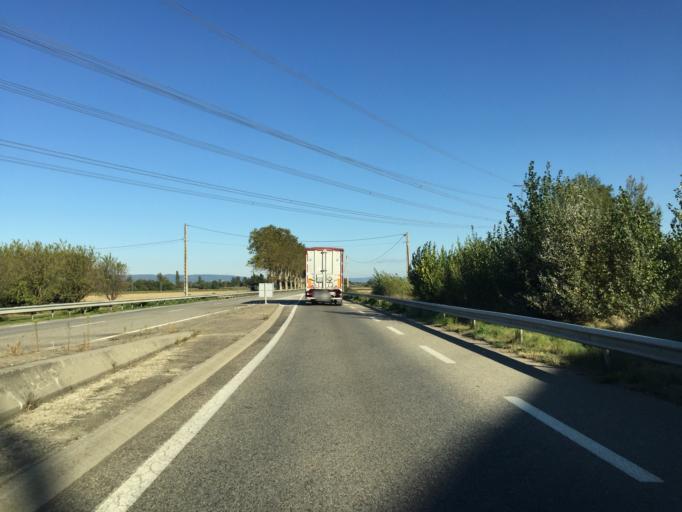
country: FR
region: Provence-Alpes-Cote d'Azur
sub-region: Departement du Vaucluse
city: Lapalud
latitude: 44.2772
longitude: 4.6983
